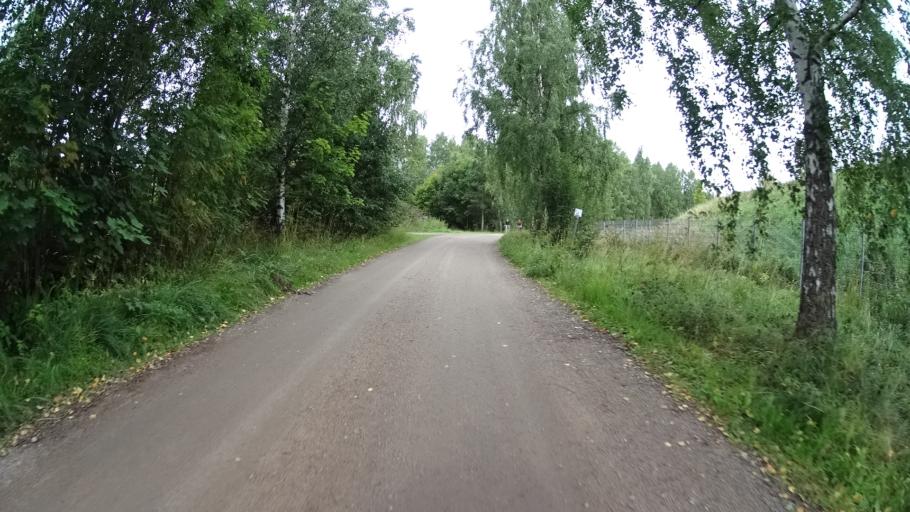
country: FI
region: Uusimaa
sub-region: Helsinki
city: Teekkarikylae
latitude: 60.2799
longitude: 24.8881
